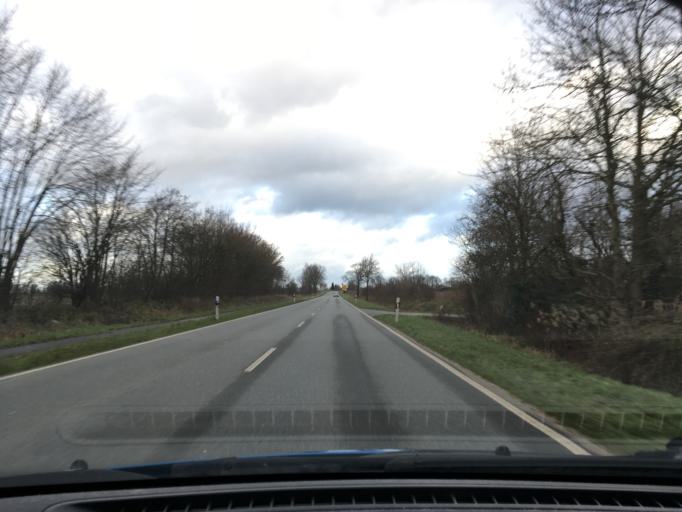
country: DE
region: Schleswig-Holstein
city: Kaisborstel
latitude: 54.0273
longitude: 9.4765
